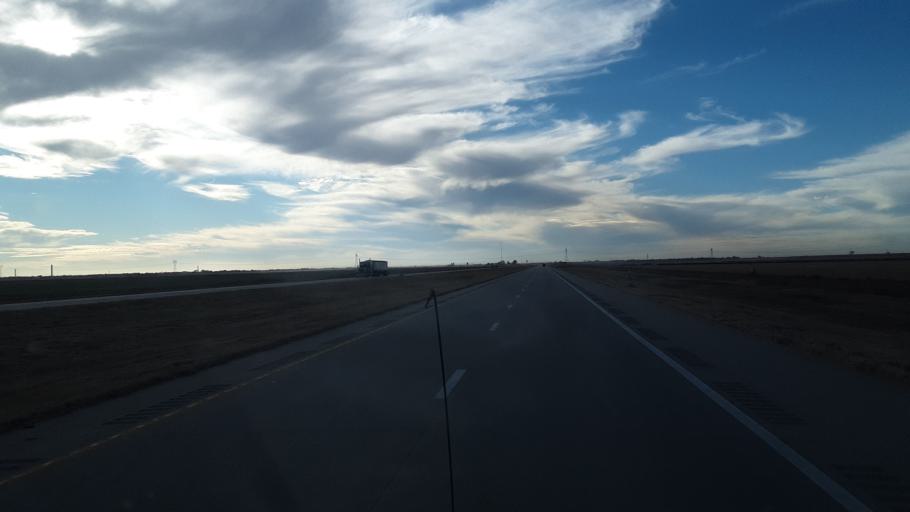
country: US
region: Kansas
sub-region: Finney County
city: Holcomb
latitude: 38.0036
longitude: -100.9498
